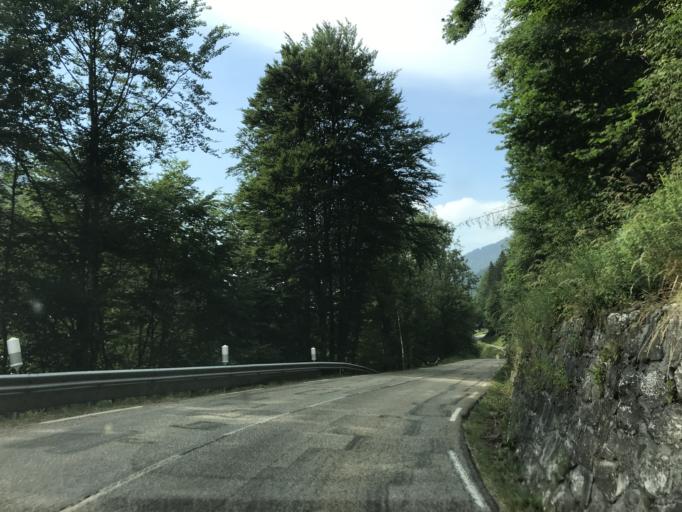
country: FR
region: Rhone-Alpes
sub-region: Departement de l'Isere
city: Allevard
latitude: 45.3623
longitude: 6.0974
